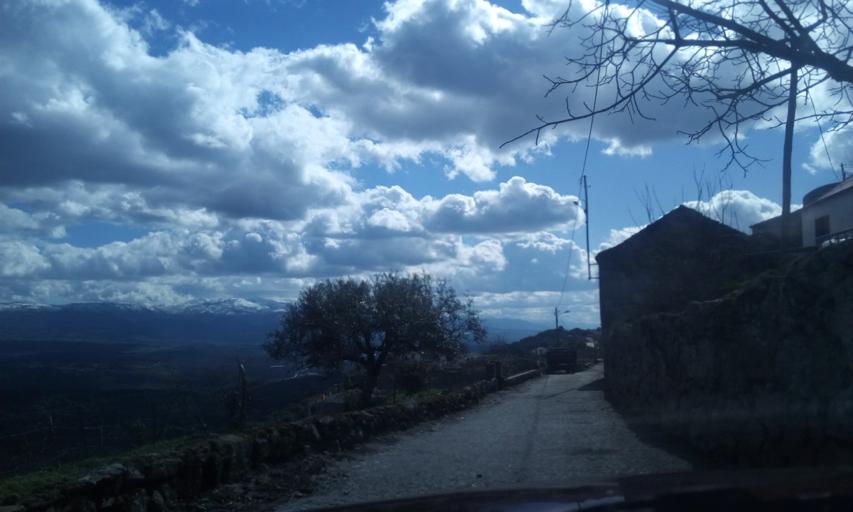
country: PT
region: Guarda
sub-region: Fornos de Algodres
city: Fornos de Algodres
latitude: 40.6477
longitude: -7.5150
